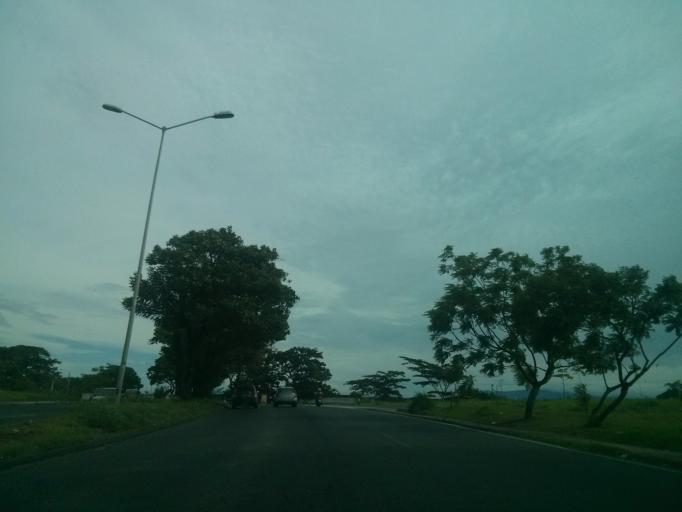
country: CR
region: San Jose
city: San Felipe
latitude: 9.9220
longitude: -84.1072
